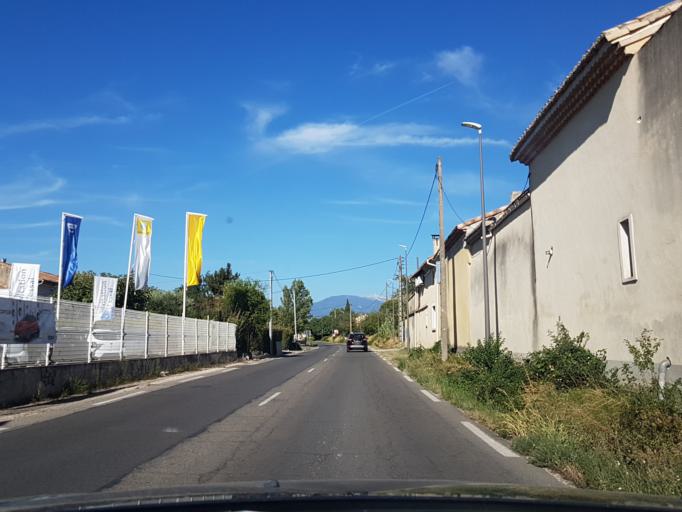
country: FR
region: Provence-Alpes-Cote d'Azur
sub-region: Departement du Vaucluse
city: Carpentras
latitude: 44.0433
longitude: 5.0256
